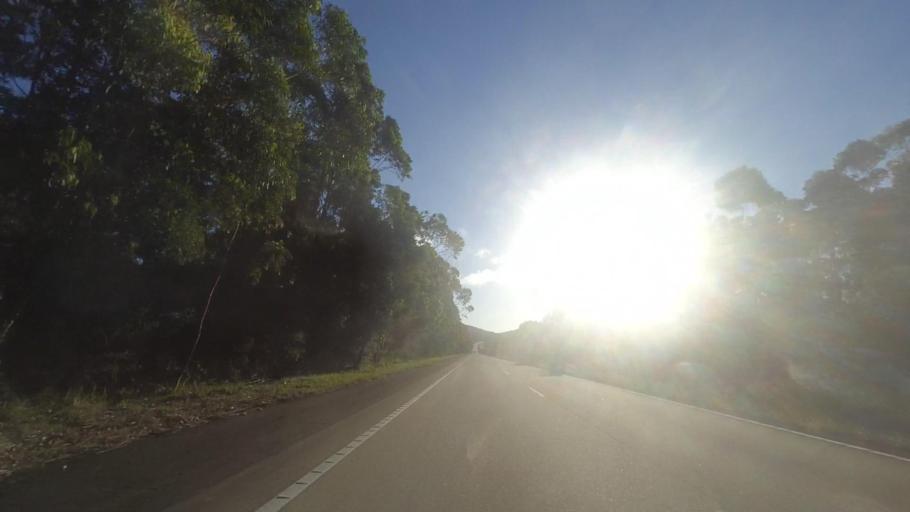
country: AU
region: New South Wales
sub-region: Great Lakes
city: Bulahdelah
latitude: -32.3785
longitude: 152.2722
